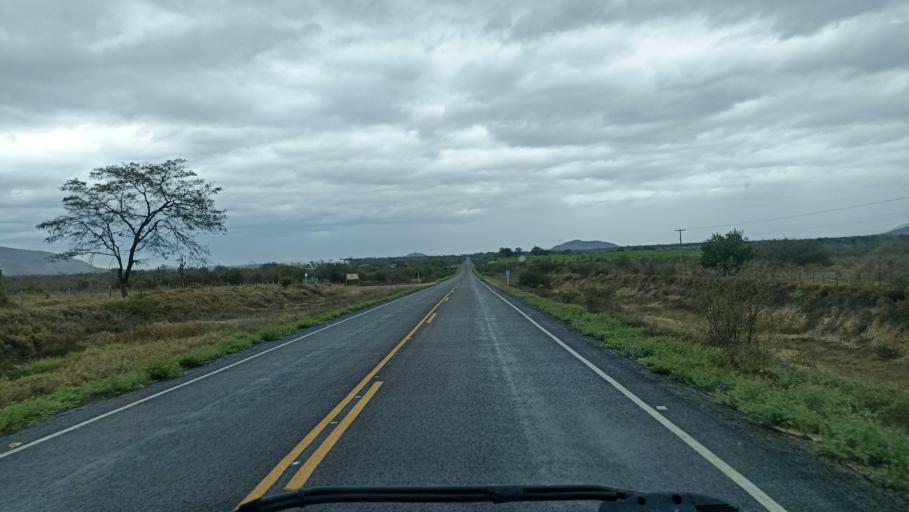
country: BR
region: Bahia
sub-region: Iacu
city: Iacu
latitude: -12.9692
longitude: -40.4971
